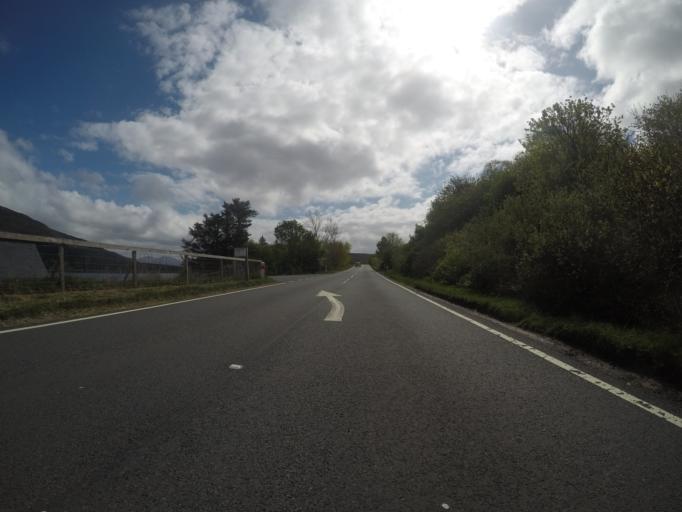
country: GB
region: Scotland
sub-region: Highland
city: Portree
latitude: 57.2792
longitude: -6.0086
